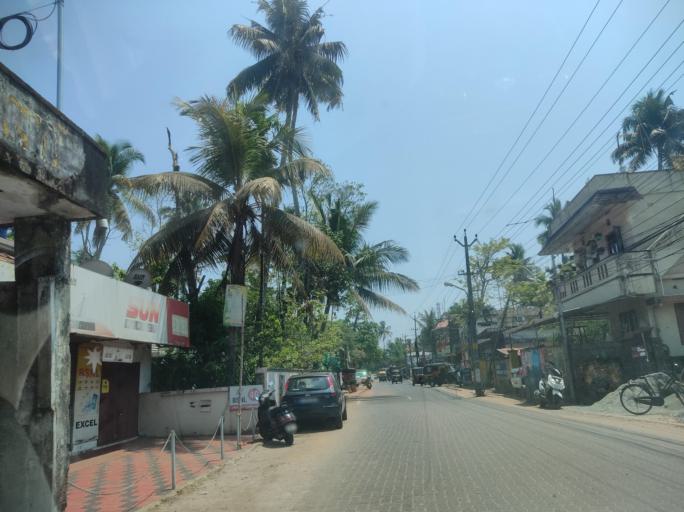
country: IN
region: Kerala
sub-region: Ernakulam
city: Cochin
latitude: 9.8937
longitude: 76.2846
